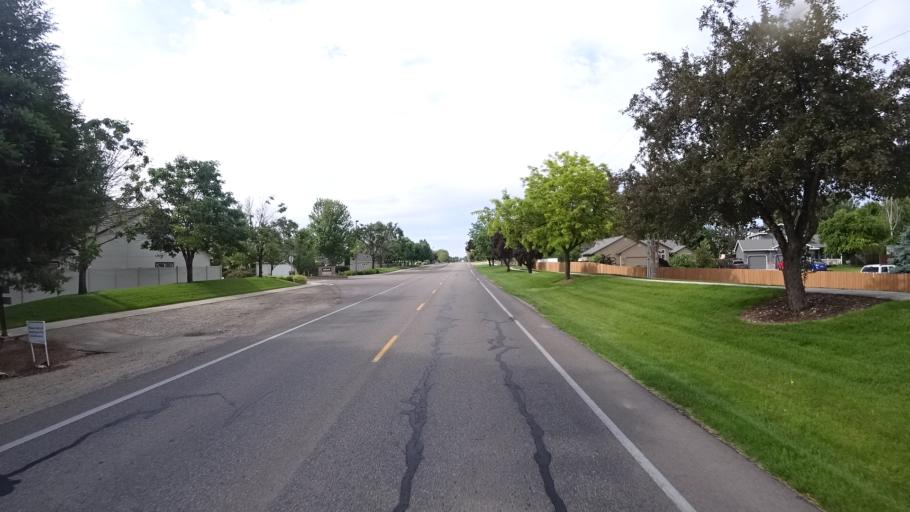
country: US
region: Idaho
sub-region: Ada County
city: Meridian
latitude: 43.5806
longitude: -116.3746
